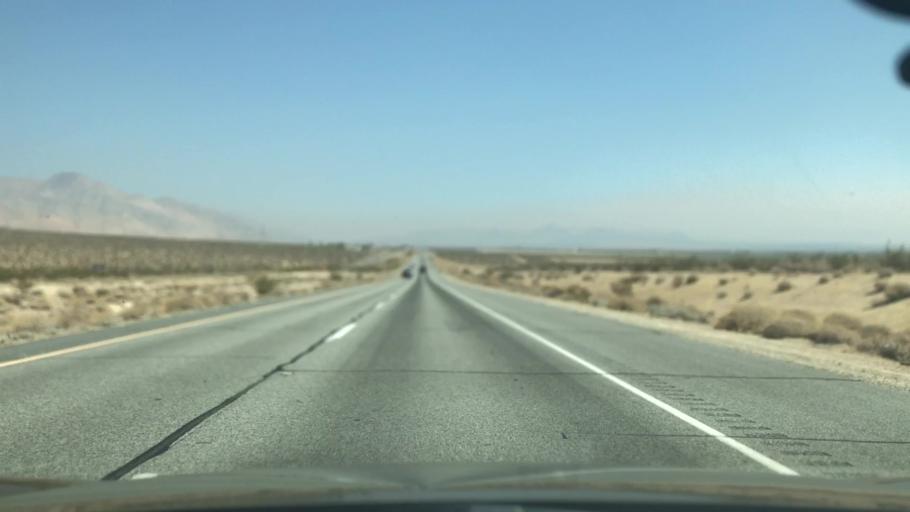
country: US
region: California
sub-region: Kern County
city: Inyokern
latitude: 35.6888
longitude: -117.8670
